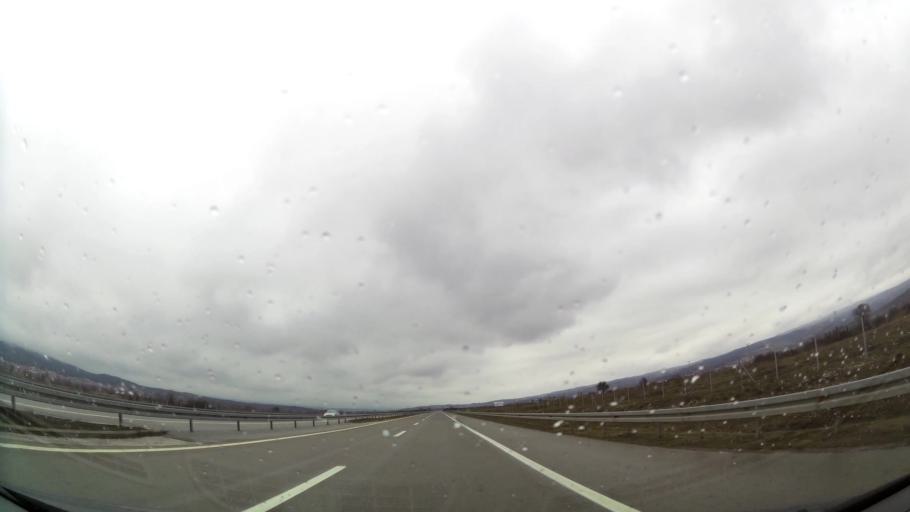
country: RS
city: Zujince
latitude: 42.3377
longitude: 21.7210
